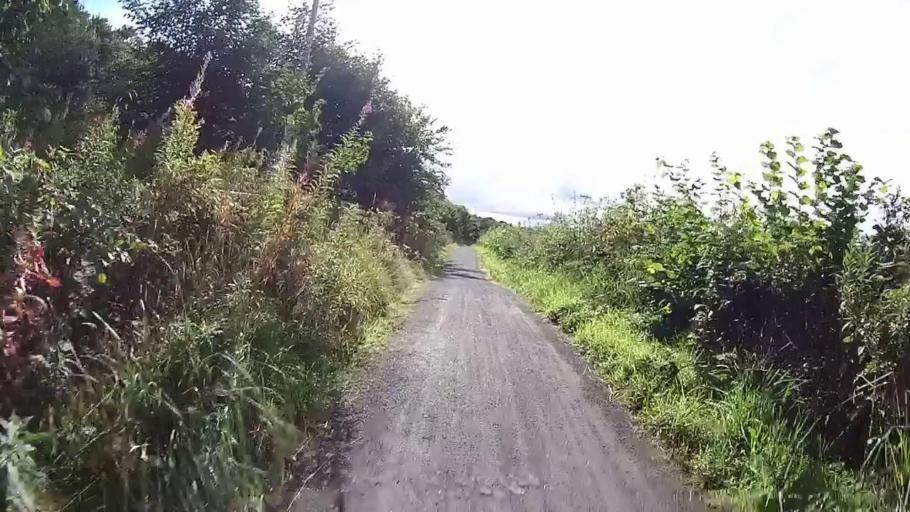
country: GB
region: Scotland
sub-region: Fife
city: Ballingry
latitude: 56.1743
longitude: -3.3601
